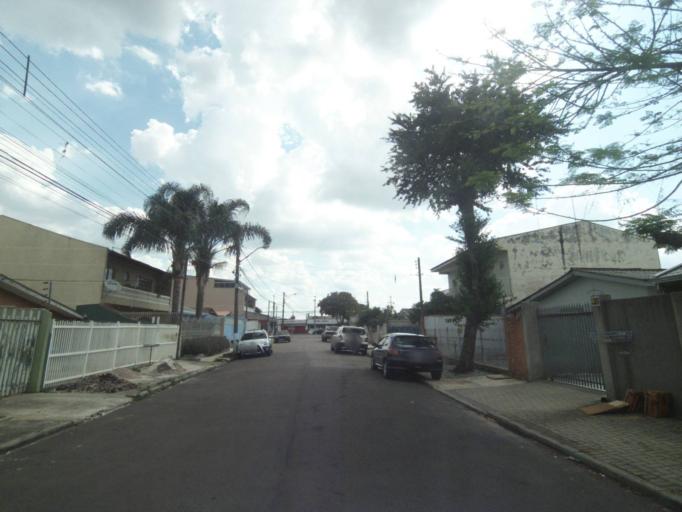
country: BR
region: Parana
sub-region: Sao Jose Dos Pinhais
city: Sao Jose dos Pinhais
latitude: -25.5305
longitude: -49.2669
